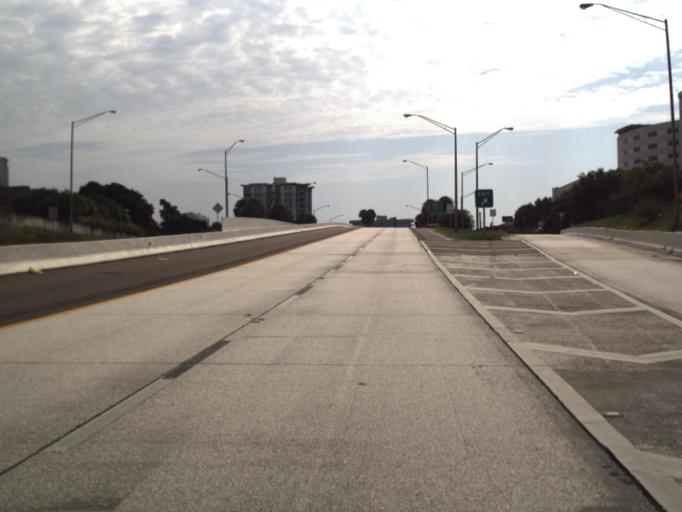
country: US
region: Florida
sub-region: Pinellas County
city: Saint Petersburg
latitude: 27.7659
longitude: -82.6445
